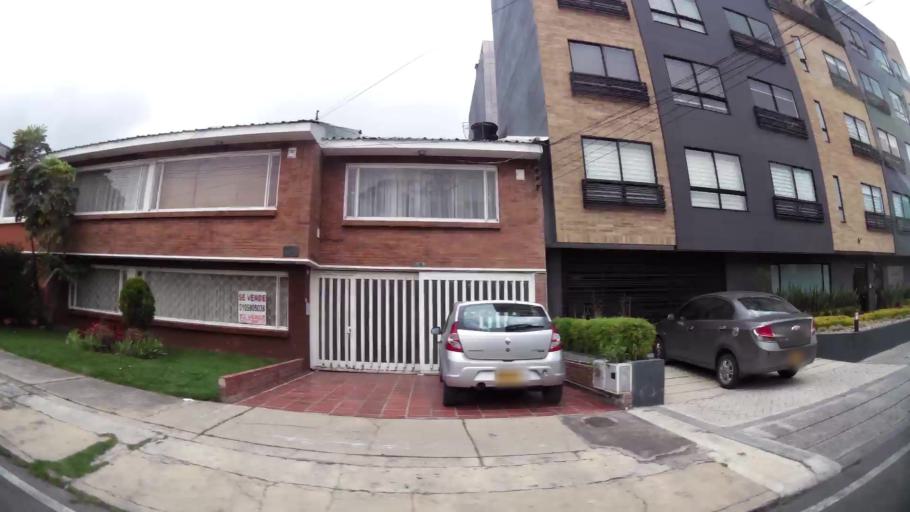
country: CO
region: Bogota D.C.
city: Barrio San Luis
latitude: 4.7246
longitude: -74.0439
